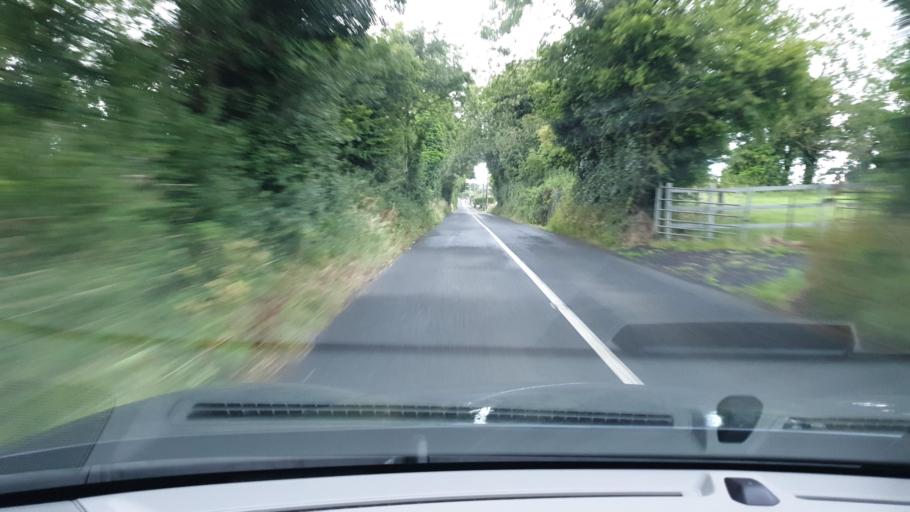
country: IE
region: Leinster
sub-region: South Dublin
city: Rathcoole
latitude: 53.2709
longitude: -6.4884
